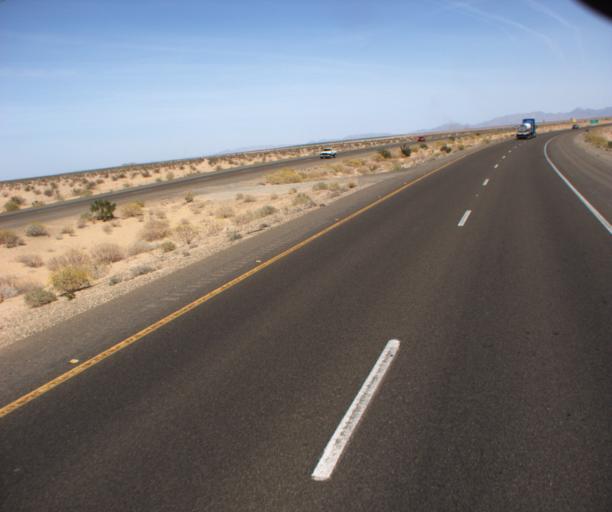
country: US
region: Arizona
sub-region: Yuma County
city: Somerton
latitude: 32.4953
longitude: -114.6583
